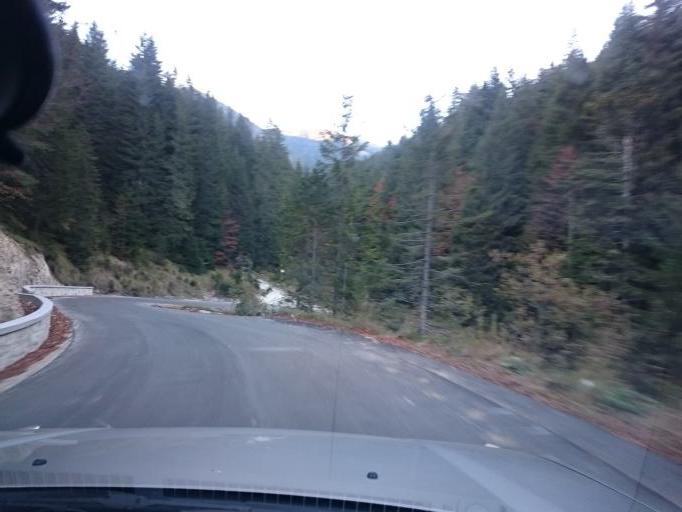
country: IT
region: Veneto
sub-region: Provincia di Vicenza
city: Roana
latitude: 45.9567
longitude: 11.4286
